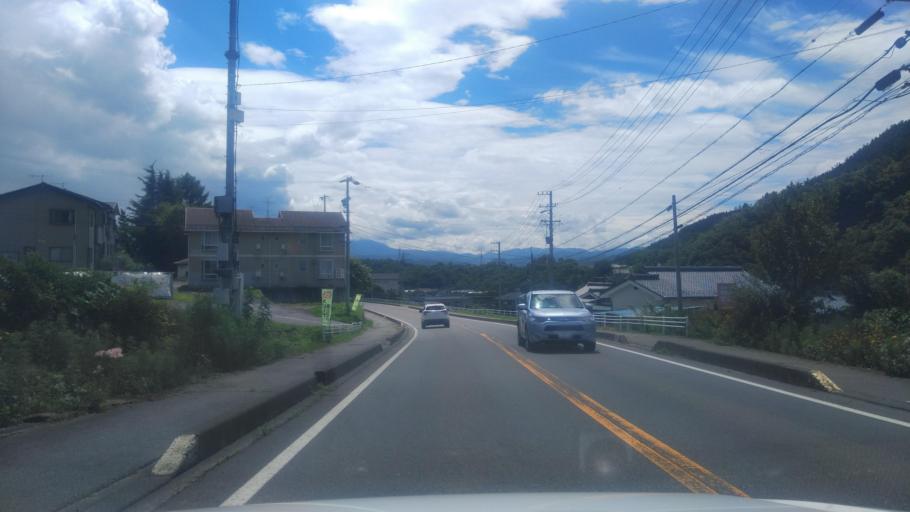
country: JP
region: Nagano
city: Ueda
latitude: 36.4290
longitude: 138.2981
